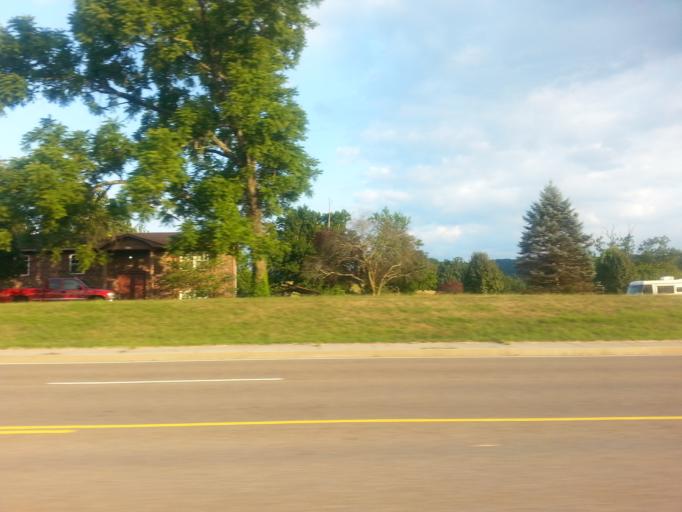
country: US
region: Tennessee
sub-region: Knox County
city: Knoxville
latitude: 36.0803
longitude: -83.9430
